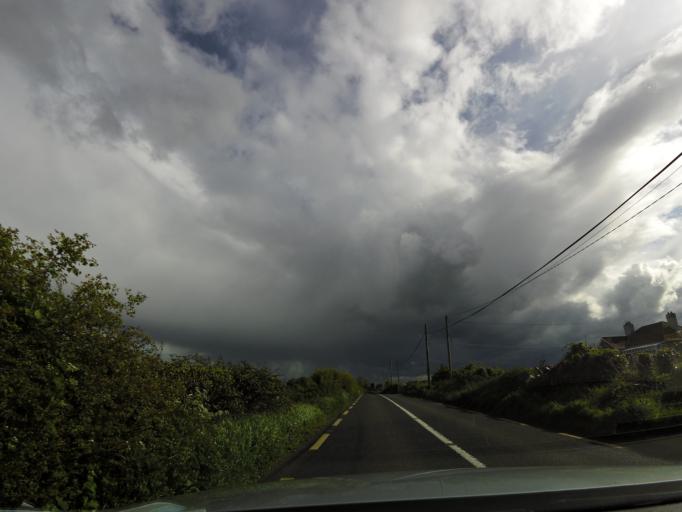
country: IE
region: Munster
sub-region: North Tipperary
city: Templemore
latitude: 52.7522
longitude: -7.8450
